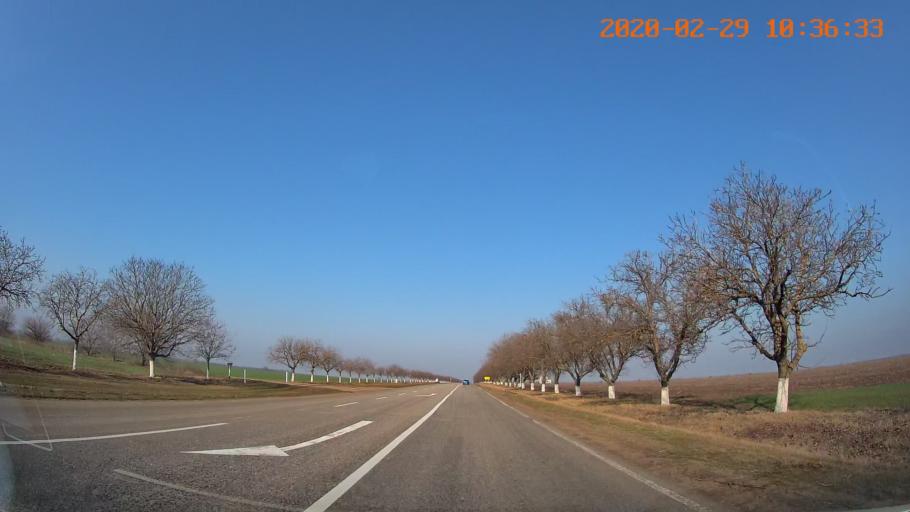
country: MD
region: Anenii Noi
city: Varnita
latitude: 46.9968
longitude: 29.5034
